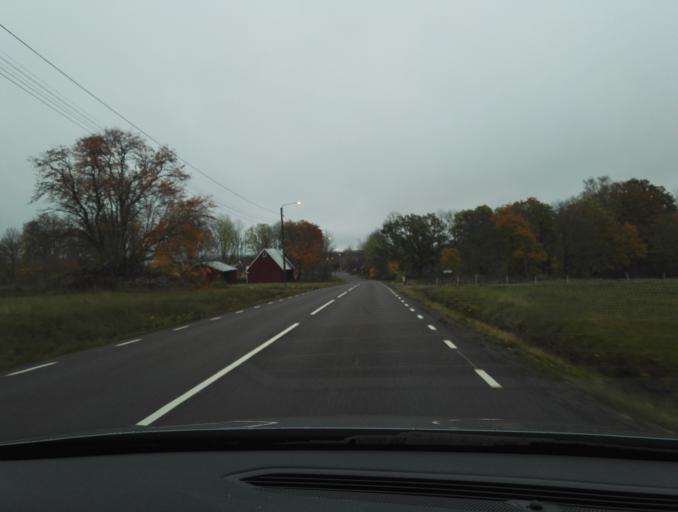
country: SE
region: Kronoberg
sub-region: Vaxjo Kommun
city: Rottne
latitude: 57.0240
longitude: 14.8443
